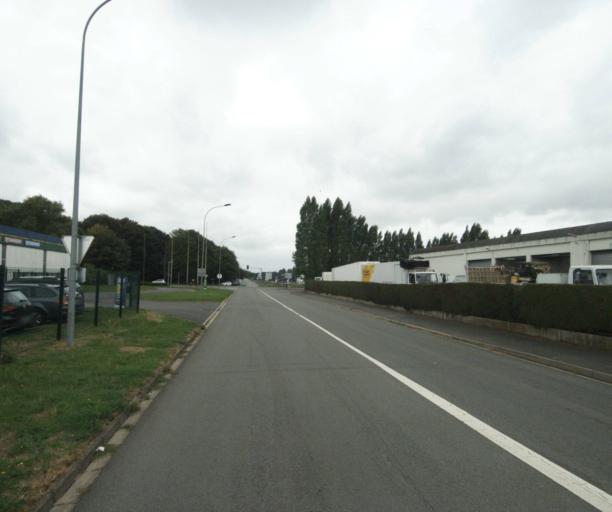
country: FR
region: Nord-Pas-de-Calais
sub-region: Departement du Nord
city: Lesquin
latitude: 50.5810
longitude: 3.1139
